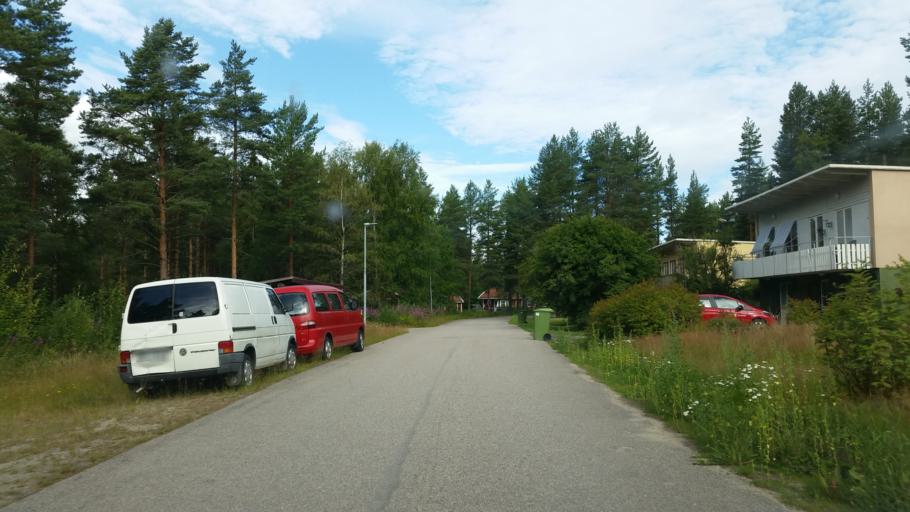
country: SE
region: Vaesternorrland
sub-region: Ange Kommun
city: Ange
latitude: 62.1853
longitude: 15.6438
